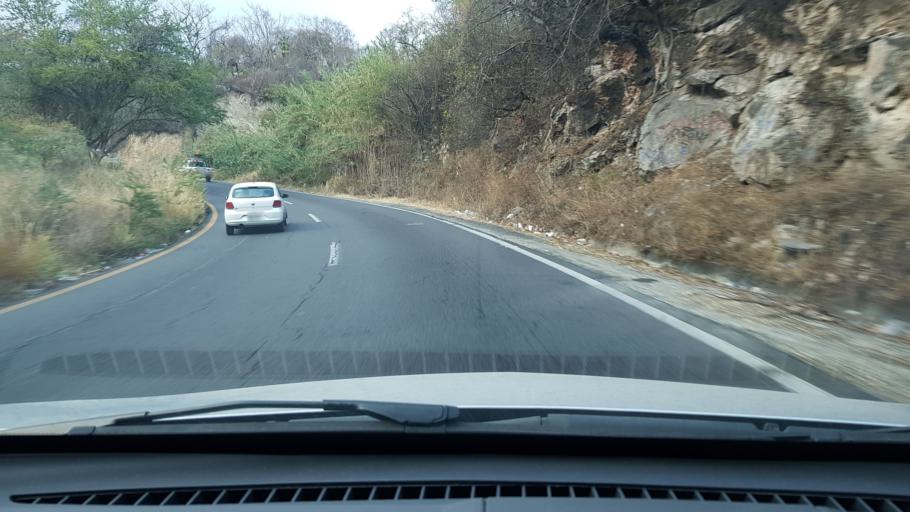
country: MX
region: Morelos
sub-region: Jiutepec
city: Independencia
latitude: 18.8736
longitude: -99.1198
